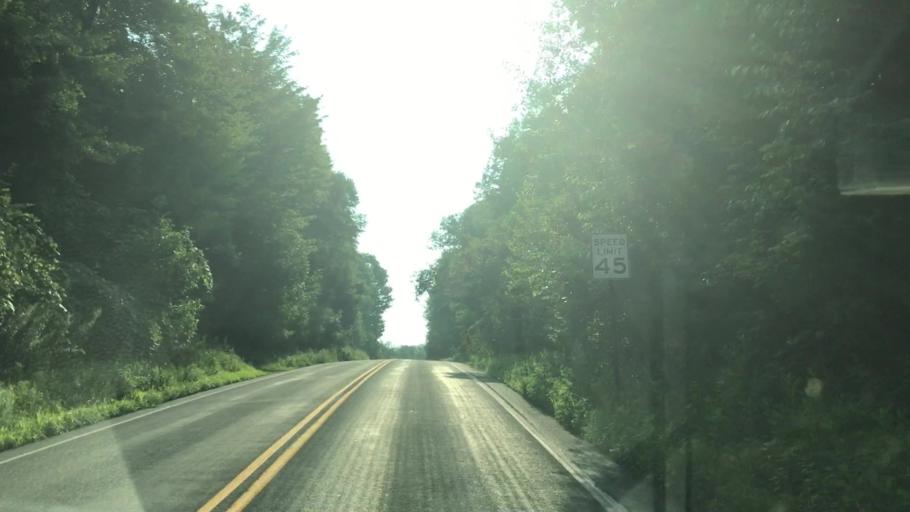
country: US
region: Pennsylvania
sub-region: Lackawanna County
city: Dalton
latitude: 41.5973
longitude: -75.6685
